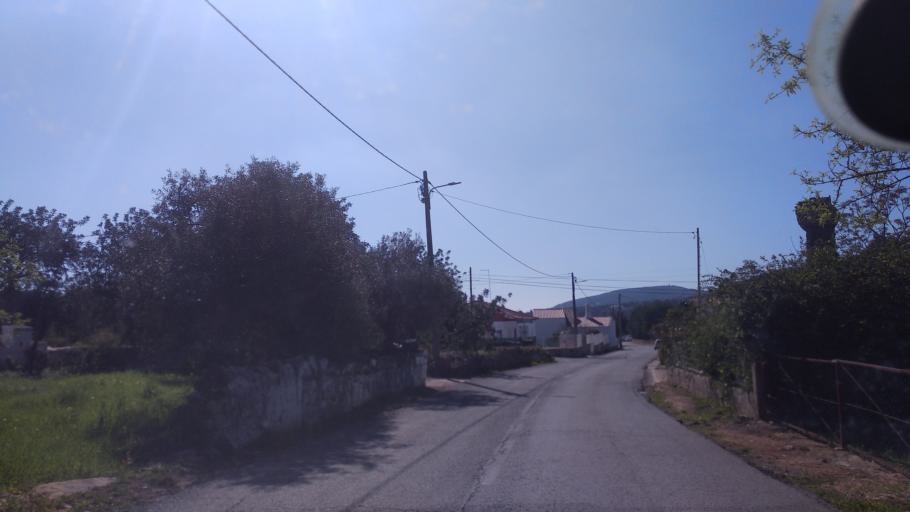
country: PT
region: Faro
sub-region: Sao Bras de Alportel
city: Sao Bras de Alportel
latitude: 37.1239
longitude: -7.9227
